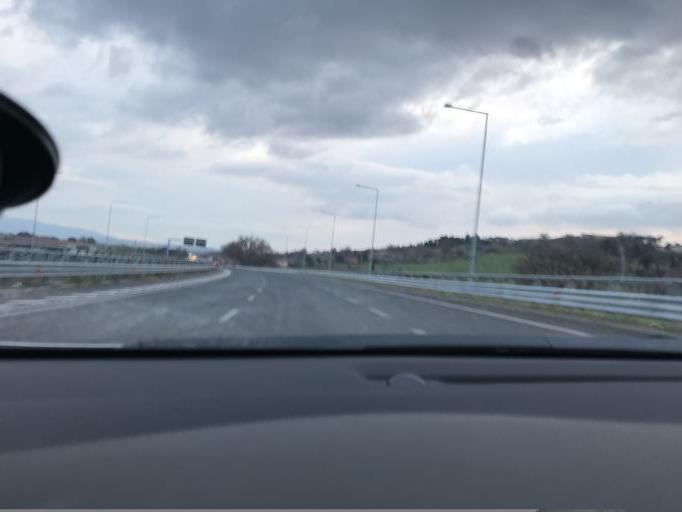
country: IT
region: Umbria
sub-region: Provincia di Perugia
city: Petrignano
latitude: 43.1346
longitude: 12.5247
